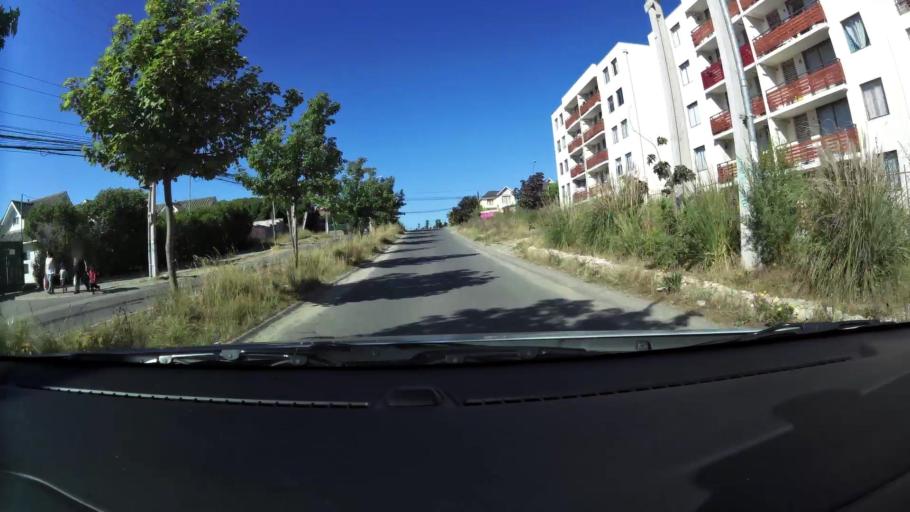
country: CL
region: Valparaiso
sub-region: Provincia de Valparaiso
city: Valparaiso
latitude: -33.1242
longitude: -71.5715
